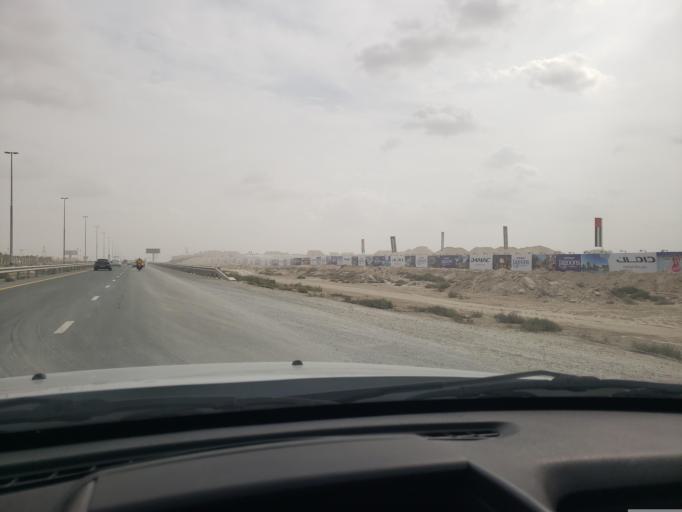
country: AE
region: Dubai
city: Dubai
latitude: 25.0132
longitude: 55.2450
